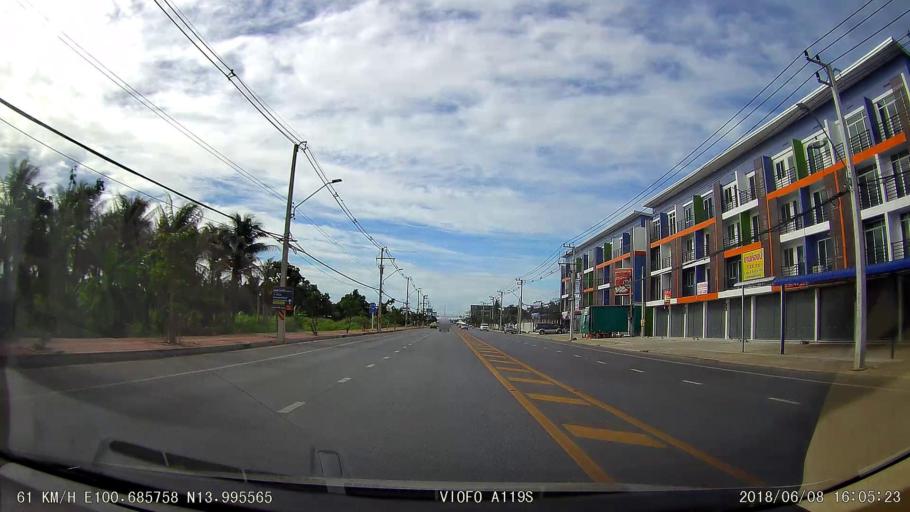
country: TH
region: Pathum Thani
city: Thanyaburi
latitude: 13.9956
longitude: 100.6858
